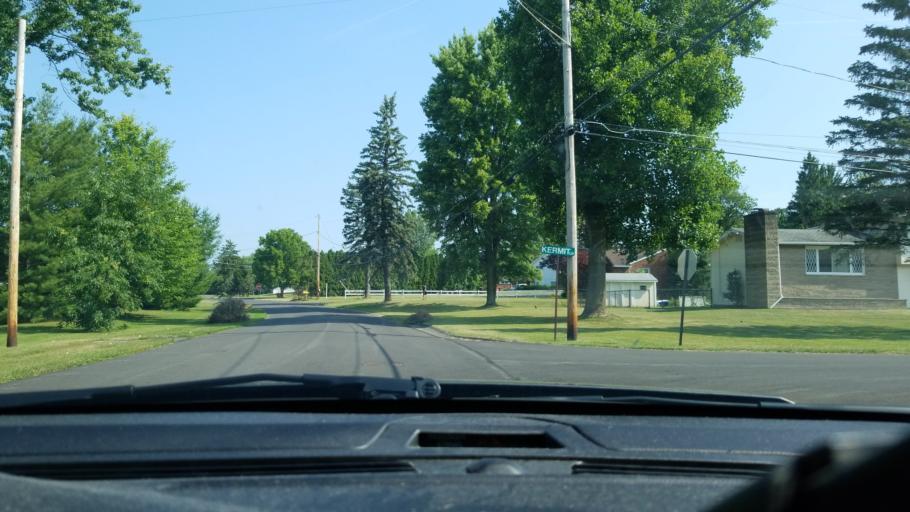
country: US
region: New York
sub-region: Onondaga County
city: East Syracuse
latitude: 43.0997
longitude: -76.0713
